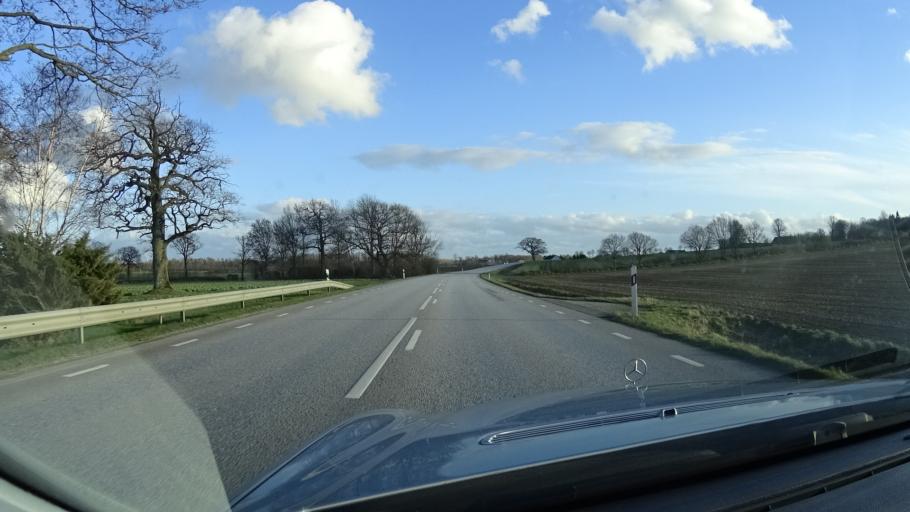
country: SE
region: Skane
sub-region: Hoors Kommun
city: Loberod
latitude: 55.8495
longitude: 13.4990
